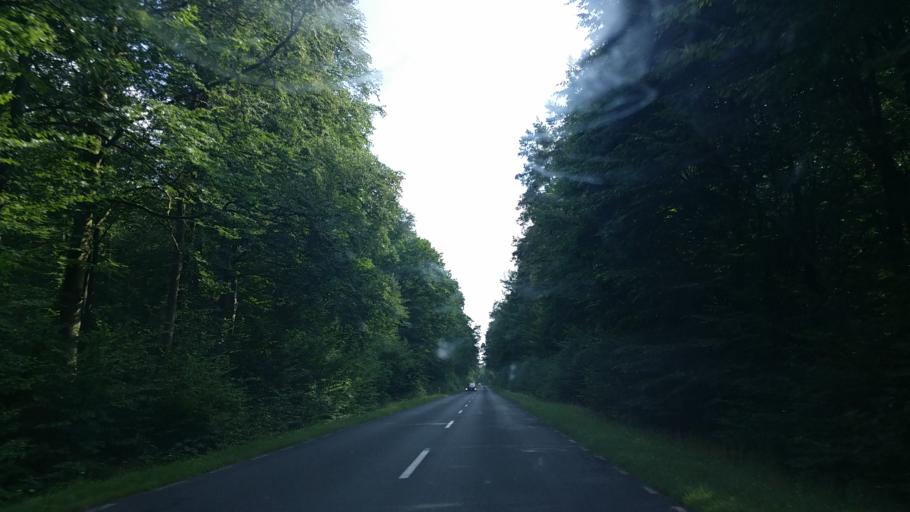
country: PL
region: Lubusz
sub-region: Powiat gorzowski
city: Klodawa
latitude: 52.8626
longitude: 15.2033
